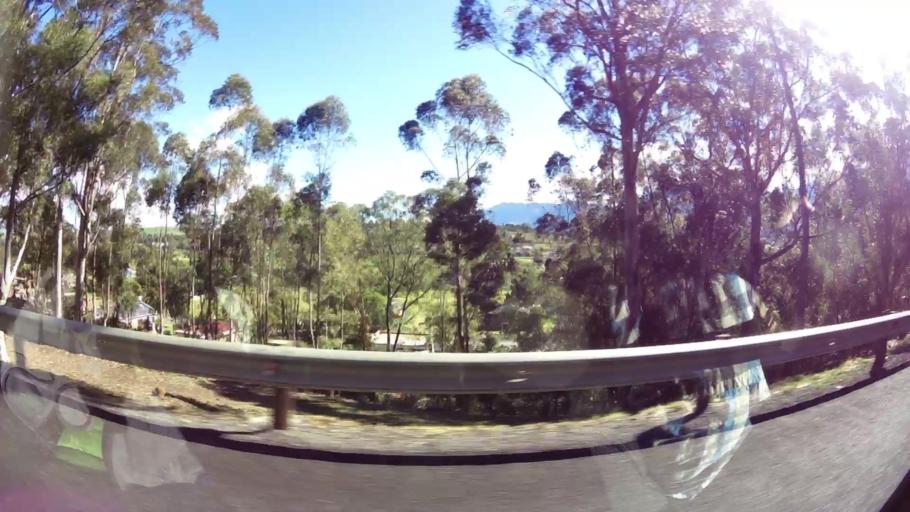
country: ZA
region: Western Cape
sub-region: Overberg District Municipality
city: Swellendam
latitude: -34.0348
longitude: 20.4359
